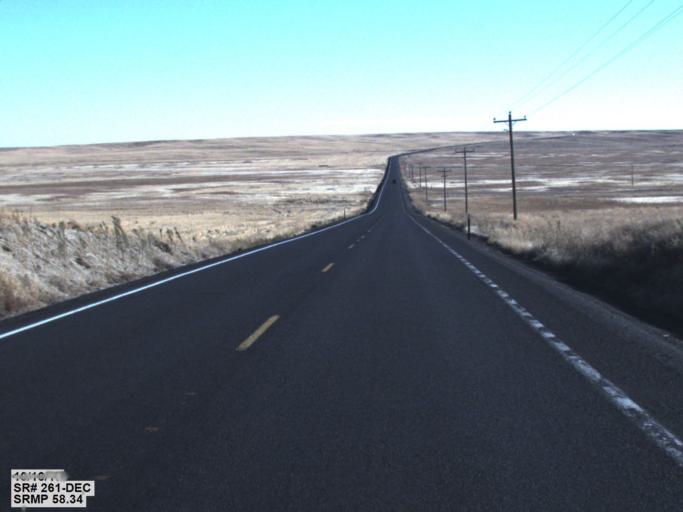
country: US
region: Washington
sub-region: Adams County
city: Ritzville
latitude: 47.0533
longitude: -118.3591
